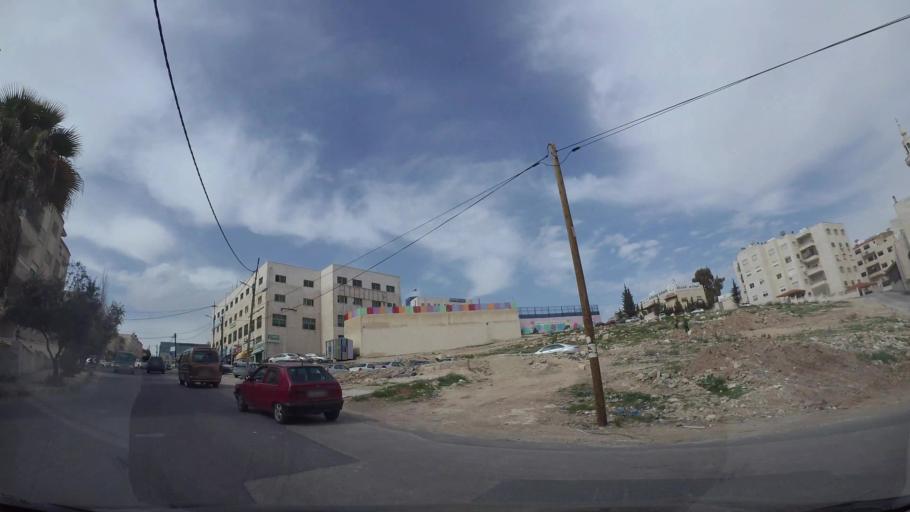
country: JO
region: Amman
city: Amman
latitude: 32.0064
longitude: 35.9373
